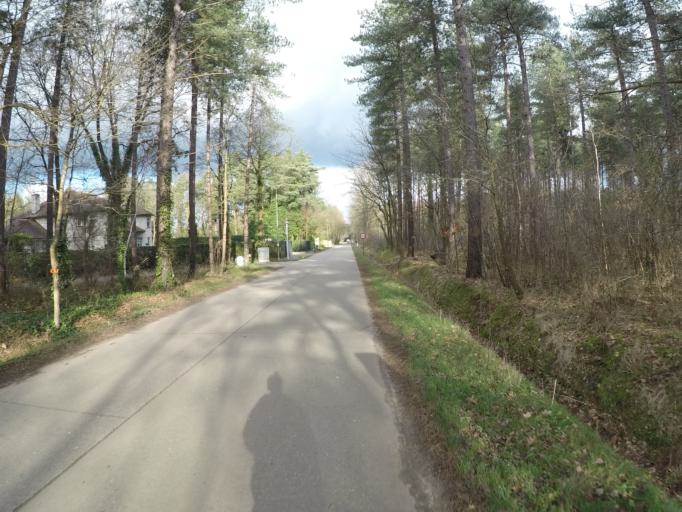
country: BE
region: Flanders
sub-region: Provincie Antwerpen
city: Vorselaar
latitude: 51.2503
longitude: 4.7758
